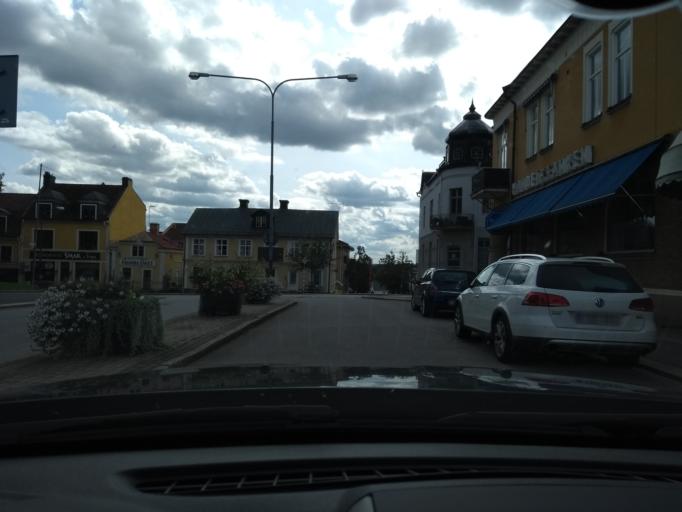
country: SE
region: Kalmar
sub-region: Vimmerby Kommun
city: Vimmerby
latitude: 57.6658
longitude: 15.8564
